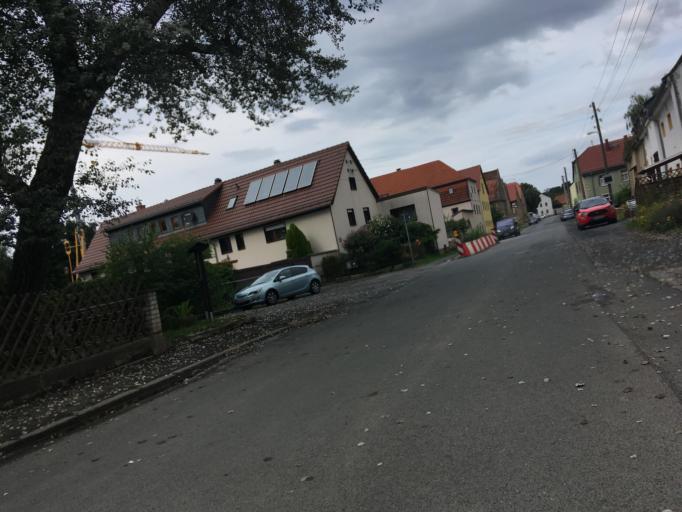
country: DE
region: Saxony
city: Dohna
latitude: 50.9377
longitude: 13.8918
